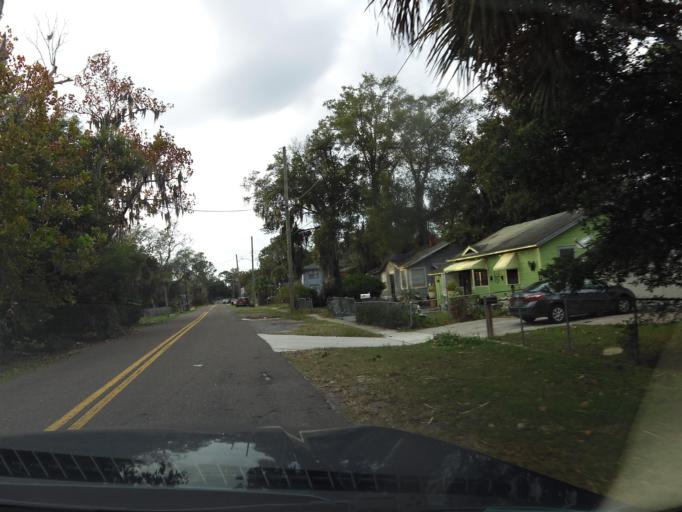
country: US
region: Florida
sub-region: Duval County
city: Jacksonville
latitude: 30.3638
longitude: -81.6594
